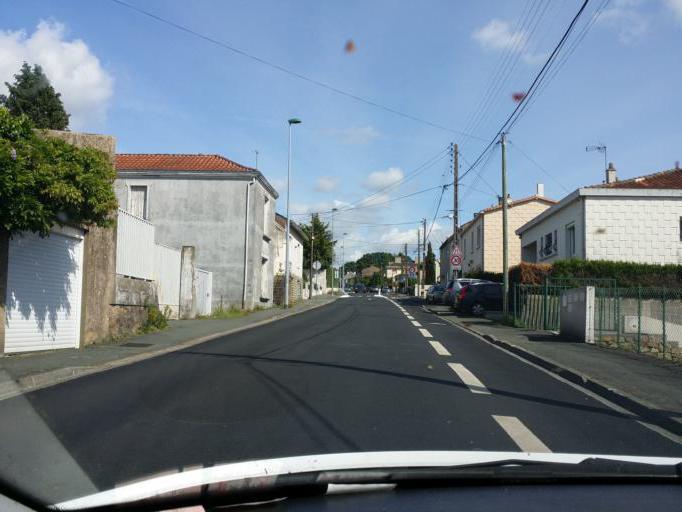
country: FR
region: Pays de la Loire
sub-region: Departement de la Vendee
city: La Roche-sur-Yon
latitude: 46.6664
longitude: -1.4191
